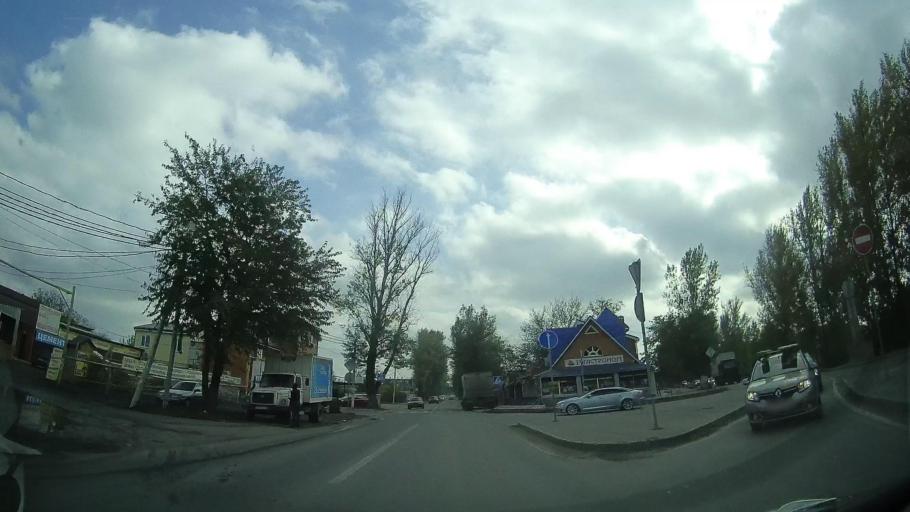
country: RU
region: Rostov
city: Severnyy
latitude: 47.2927
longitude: 39.6607
